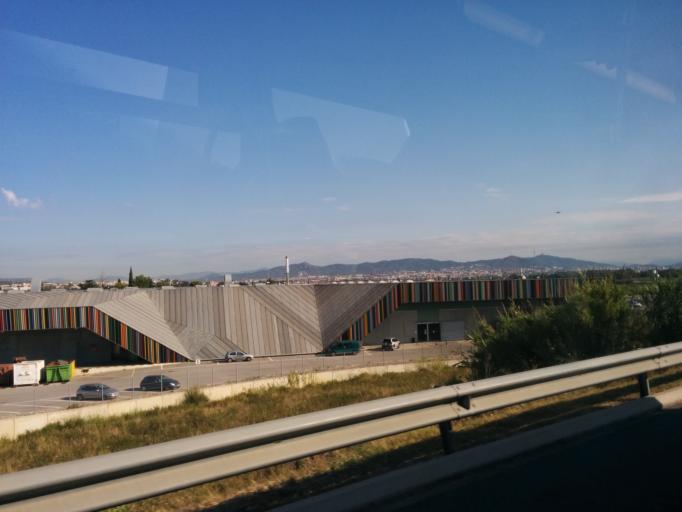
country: ES
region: Catalonia
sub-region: Provincia de Barcelona
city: El Prat de Llobregat
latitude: 41.3034
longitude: 2.0583
